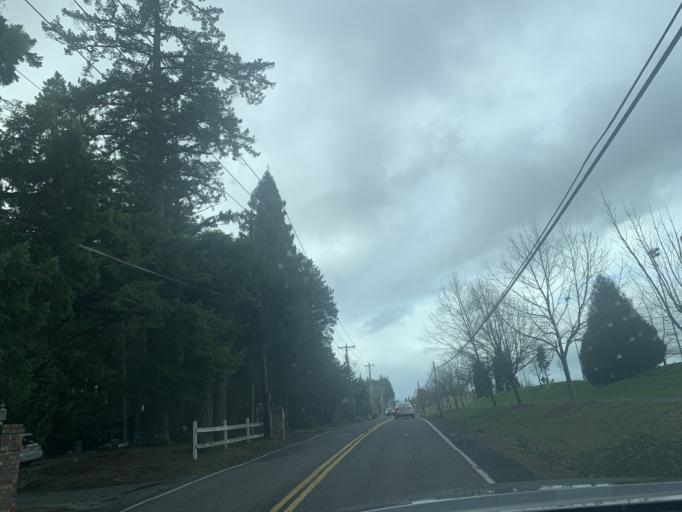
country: US
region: Oregon
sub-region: Washington County
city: Bethany
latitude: 45.5630
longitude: -122.8537
